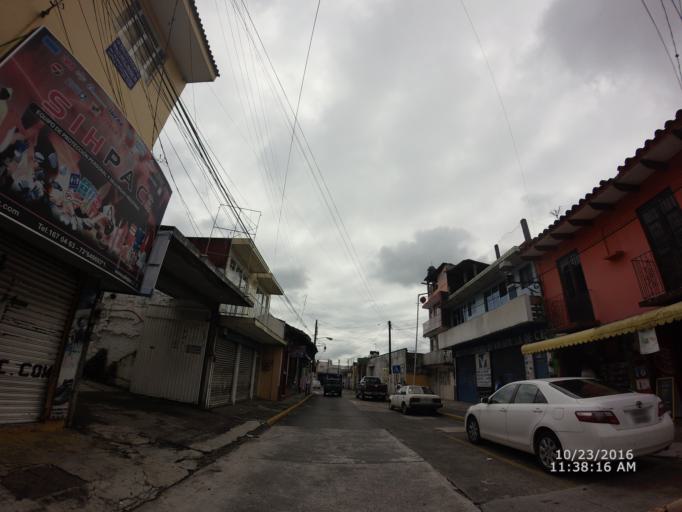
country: MX
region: Veracruz
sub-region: Xalapa
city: Xalapa de Enriquez
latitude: 19.5332
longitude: -96.9264
